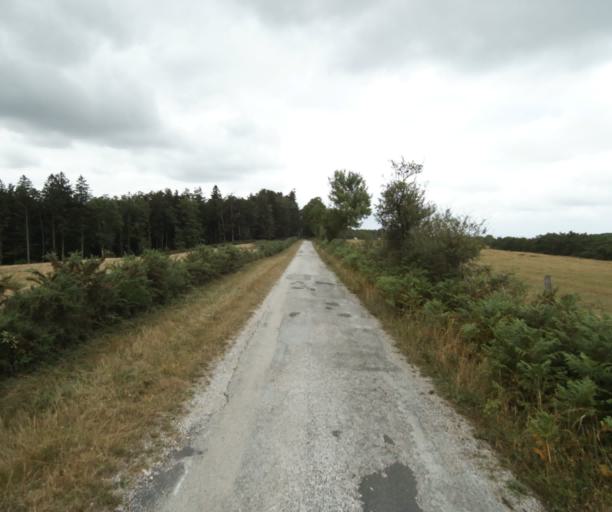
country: FR
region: Midi-Pyrenees
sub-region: Departement du Tarn
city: Soreze
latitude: 43.4241
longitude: 2.0977
